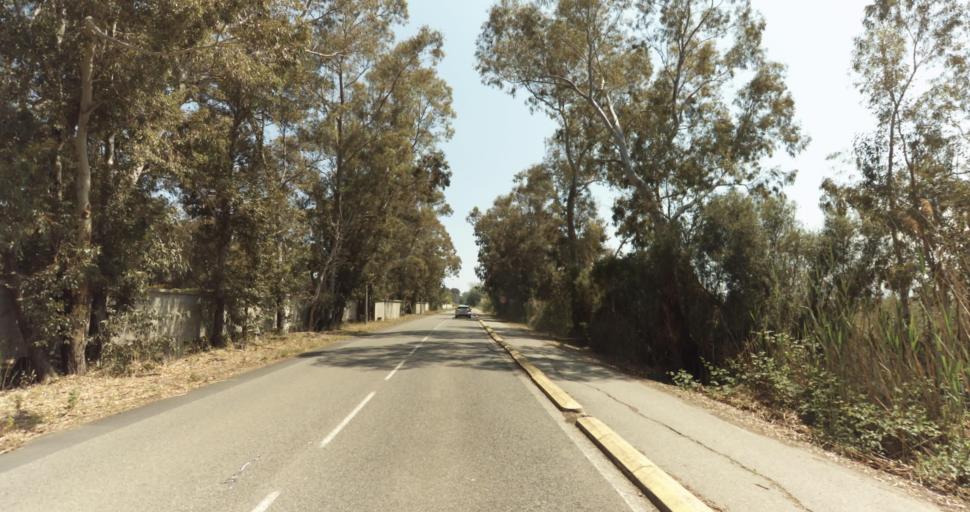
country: FR
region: Corsica
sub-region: Departement de la Haute-Corse
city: Biguglia
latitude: 42.6122
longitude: 9.4814
